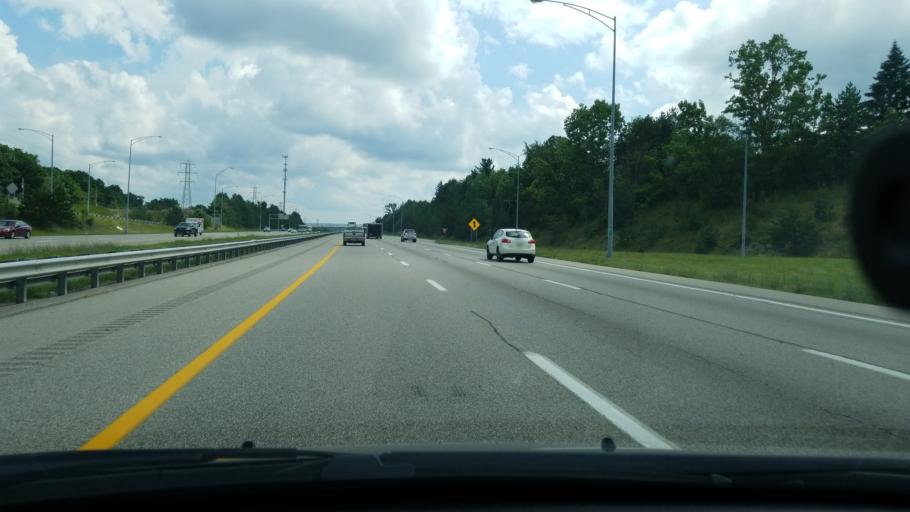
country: US
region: Ohio
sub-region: Cuyahoga County
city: Independence
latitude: 41.3431
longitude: -81.6500
